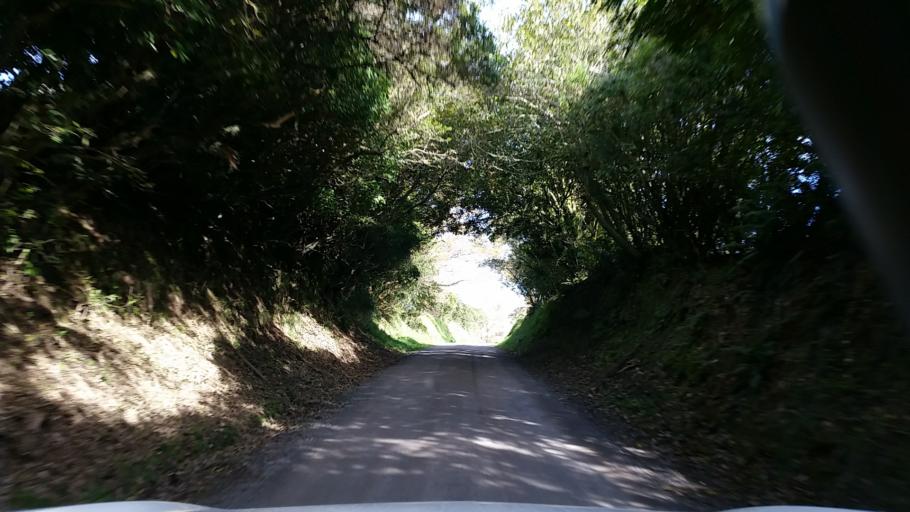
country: NZ
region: Bay of Plenty
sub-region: Rotorua District
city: Rotorua
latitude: -38.2428
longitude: 176.3443
